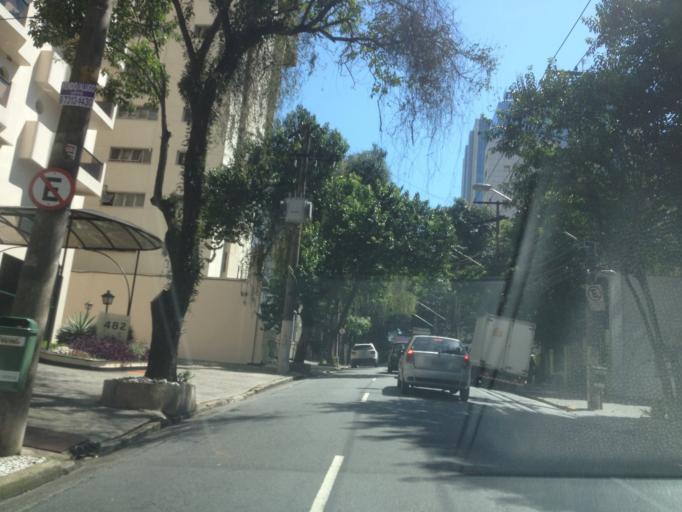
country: BR
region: Sao Paulo
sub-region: Sao Paulo
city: Sao Paulo
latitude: -23.5625
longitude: -46.6606
